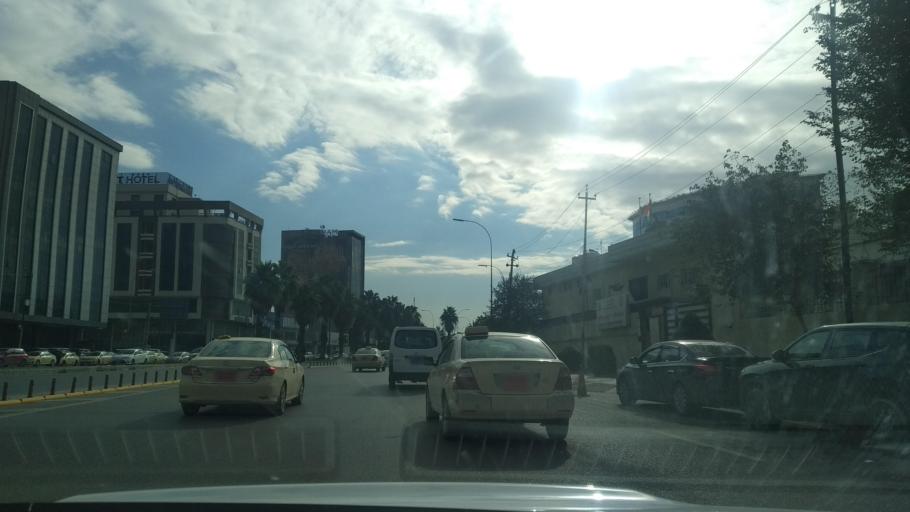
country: IQ
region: Arbil
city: Erbil
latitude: 36.2001
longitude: 44.0216
